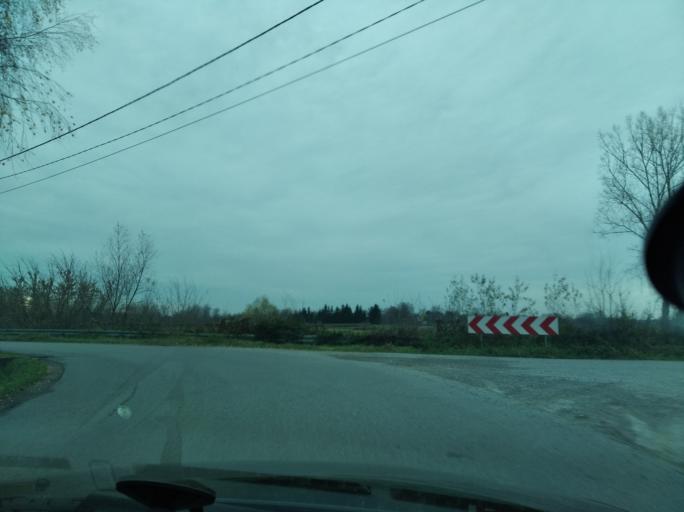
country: PL
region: Subcarpathian Voivodeship
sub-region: Powiat lancucki
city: Czarna
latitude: 50.1004
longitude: 22.2017
